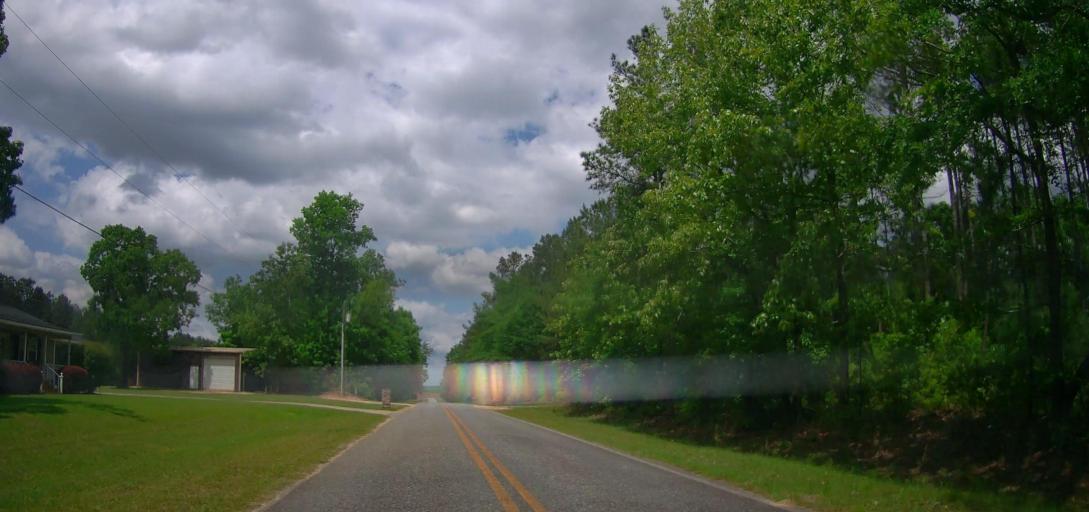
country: US
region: Georgia
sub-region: Laurens County
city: Dublin
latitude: 32.6056
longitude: -82.9378
